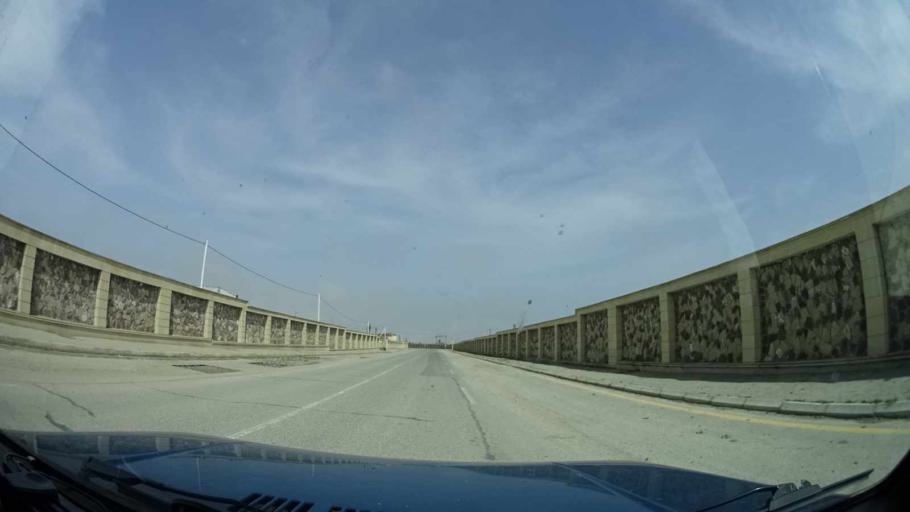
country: AZ
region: Xizi
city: Kilyazi
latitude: 40.8664
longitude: 49.3448
